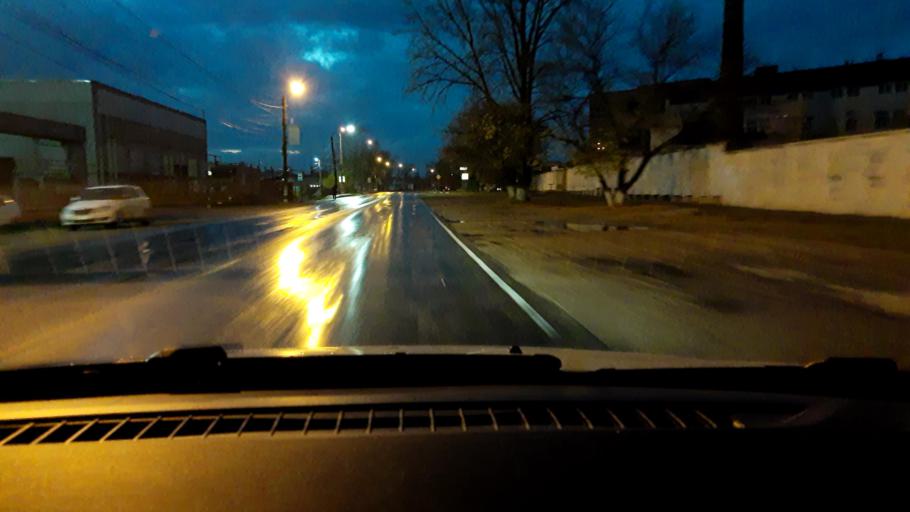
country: RU
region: Nizjnij Novgorod
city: Bor
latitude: 56.3458
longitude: 44.0864
